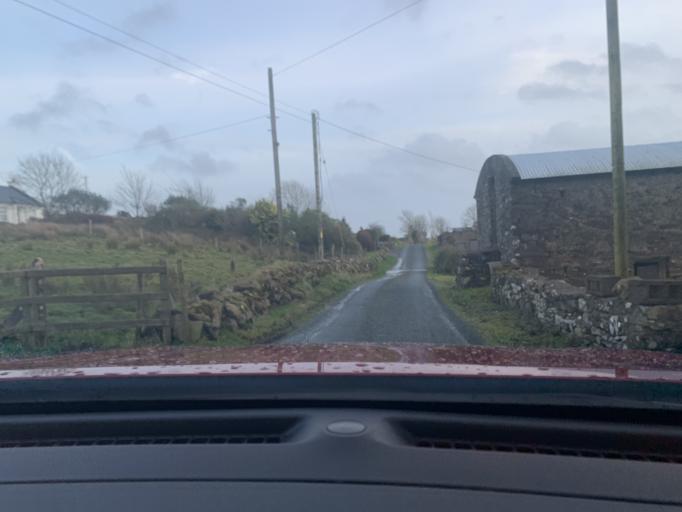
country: IE
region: Connaught
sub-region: Roscommon
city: Ballaghaderreen
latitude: 53.9526
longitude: -8.5228
